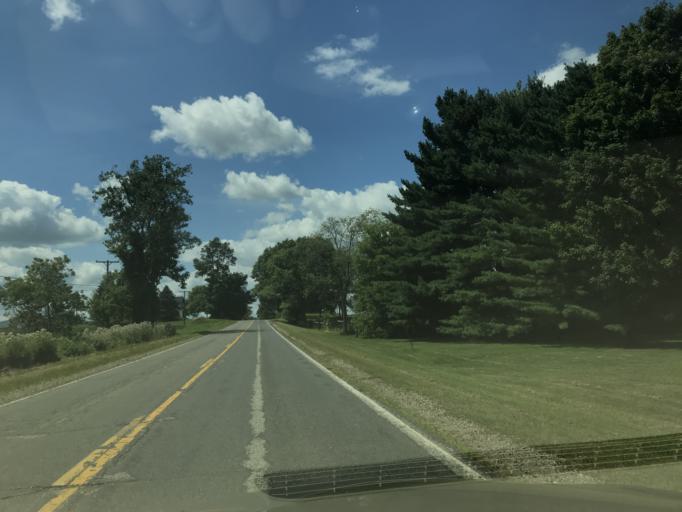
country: US
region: Michigan
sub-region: Ingham County
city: Leslie
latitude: 42.4512
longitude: -84.4524
